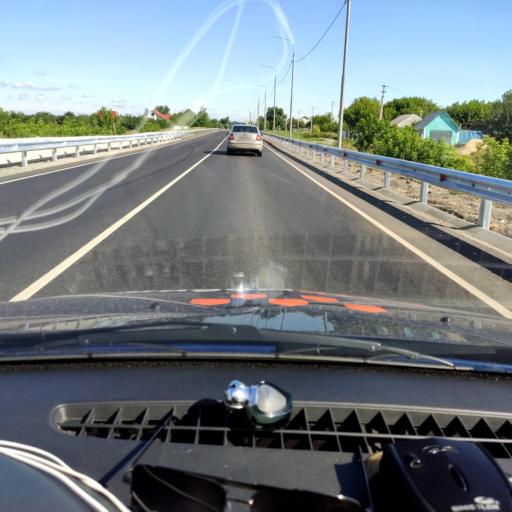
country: RU
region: Lipetsk
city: Khlevnoye
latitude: 52.1217
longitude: 39.1659
